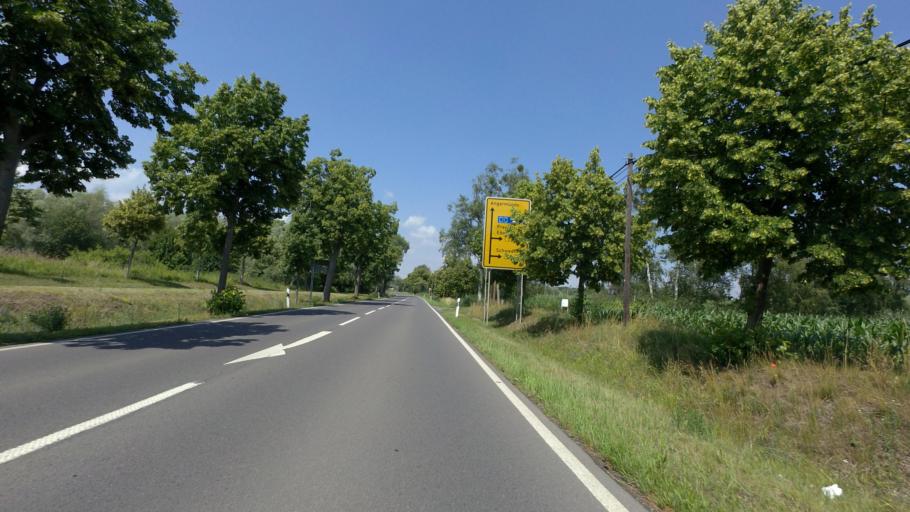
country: DE
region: Brandenburg
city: Angermunde
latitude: 53.0046
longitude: 14.0030
